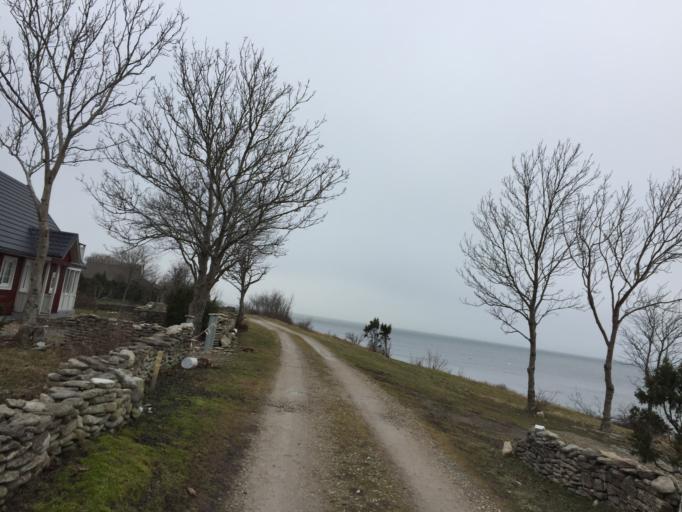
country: EE
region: Saare
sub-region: Kuressaare linn
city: Kuressaare
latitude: 58.5459
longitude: 22.2154
